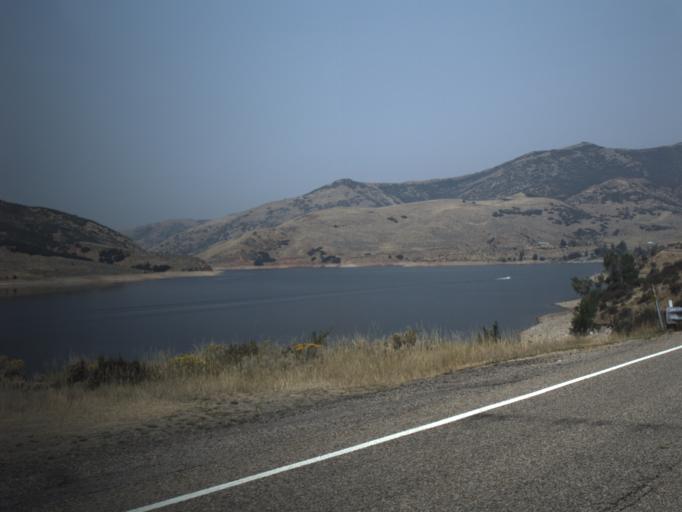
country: US
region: Utah
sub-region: Morgan County
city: Morgan
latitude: 40.9068
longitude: -111.5871
